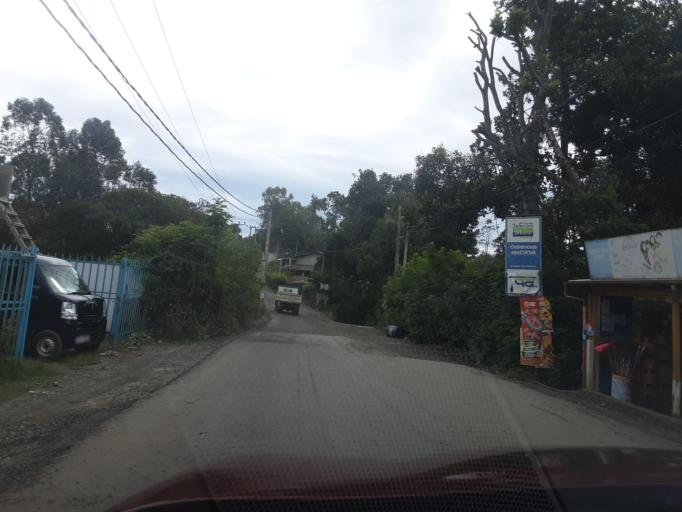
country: LK
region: Uva
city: Haputale
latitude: 6.8355
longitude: 80.9953
